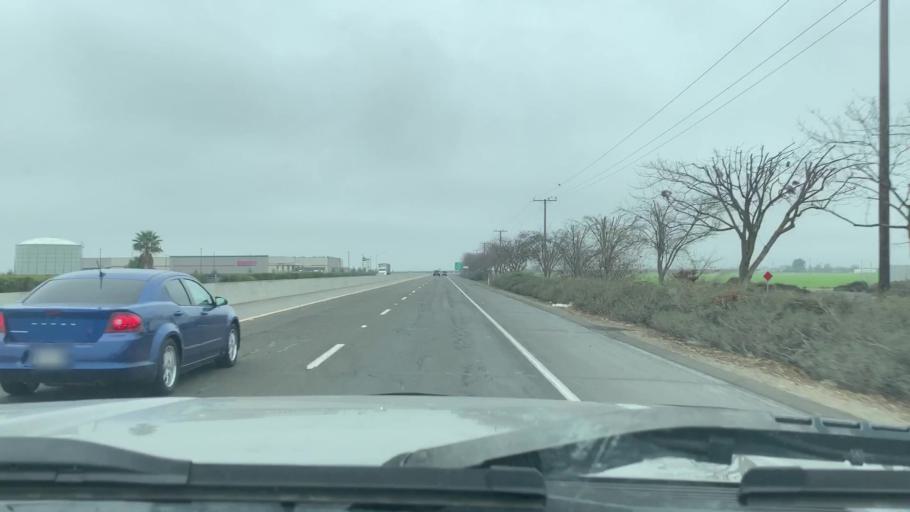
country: US
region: California
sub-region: Kings County
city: Home Garden
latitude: 36.3249
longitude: -119.6110
